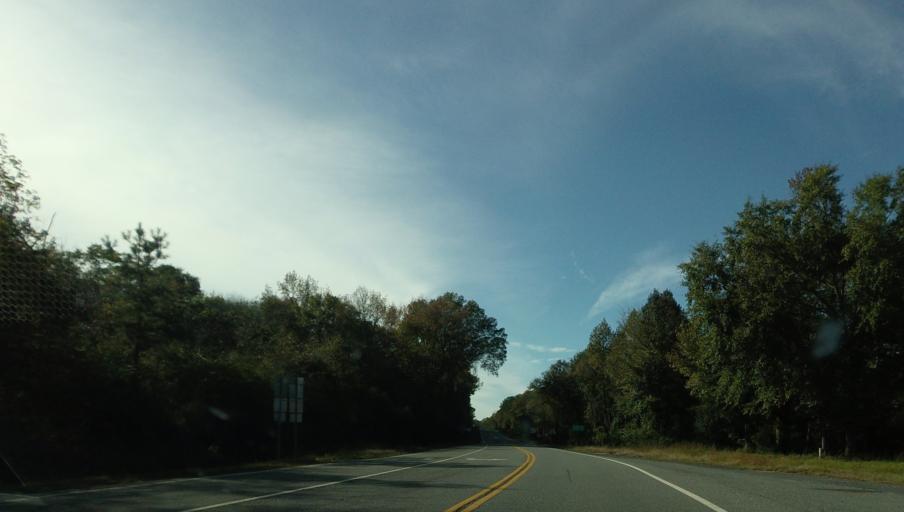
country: US
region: Georgia
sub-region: Taylor County
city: Butler
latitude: 32.7139
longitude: -84.2359
